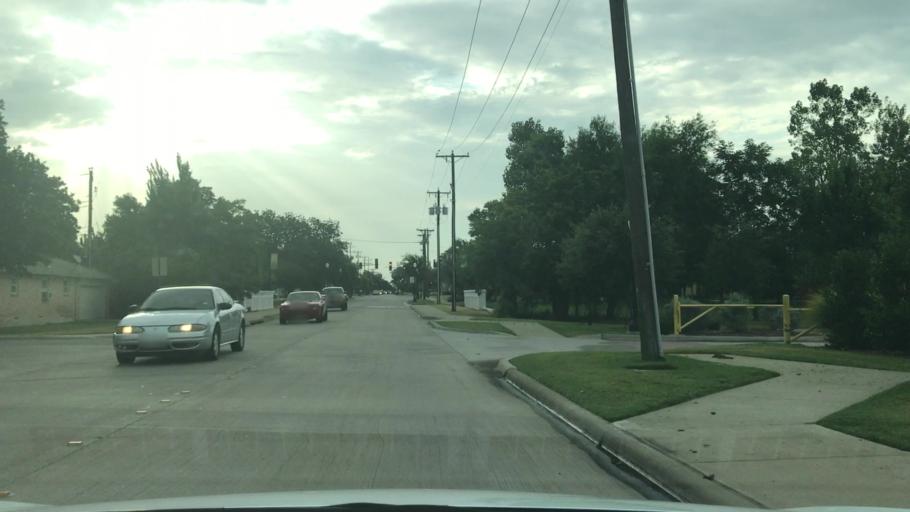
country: US
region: Texas
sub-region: Dallas County
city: Coppell
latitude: 32.9547
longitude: -97.0086
